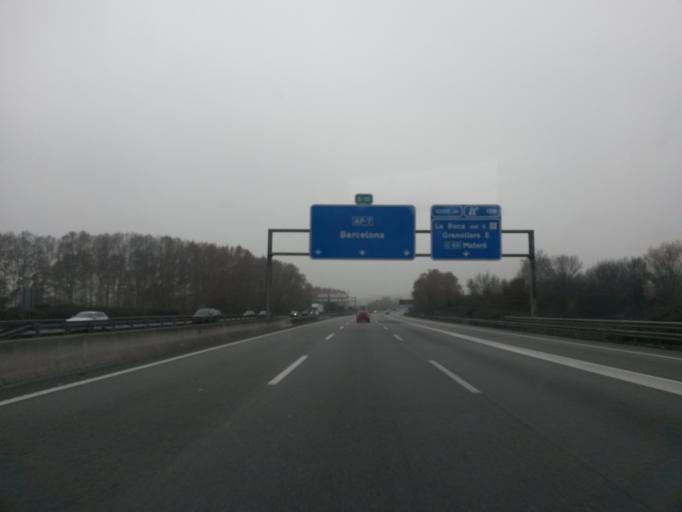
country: ES
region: Catalonia
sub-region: Provincia de Barcelona
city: La Roca del Valles
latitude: 41.6108
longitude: 2.3465
